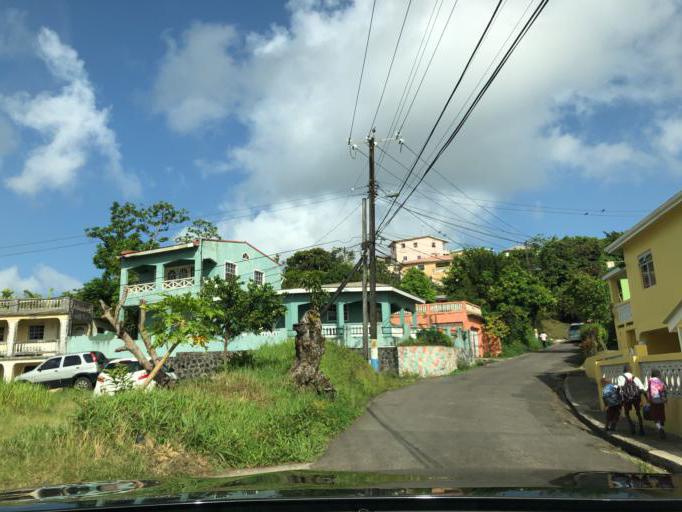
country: LC
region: Castries Quarter
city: Bisee
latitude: 13.9919
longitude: -60.9658
